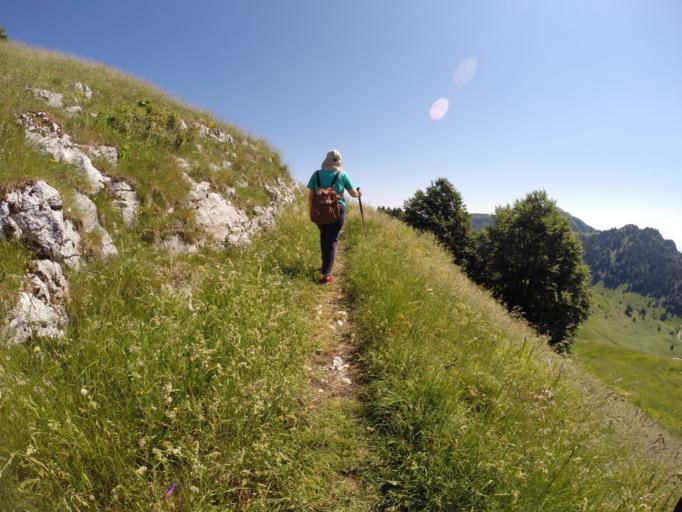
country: IT
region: Veneto
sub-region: Provincia di Treviso
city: Crespano del Grappa
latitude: 45.8847
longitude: 11.8069
